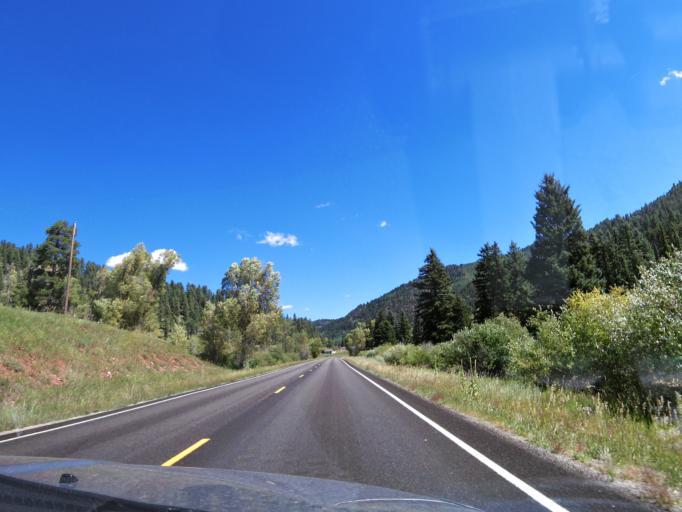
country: US
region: Colorado
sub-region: Montezuma County
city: Mancos
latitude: 37.6067
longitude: -108.1007
